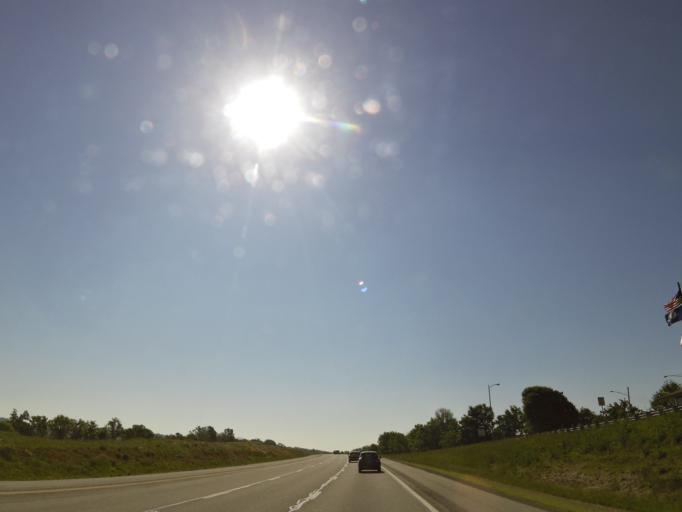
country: US
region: Kentucky
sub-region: Shelby County
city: Shelbyville
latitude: 38.1714
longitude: -85.1557
